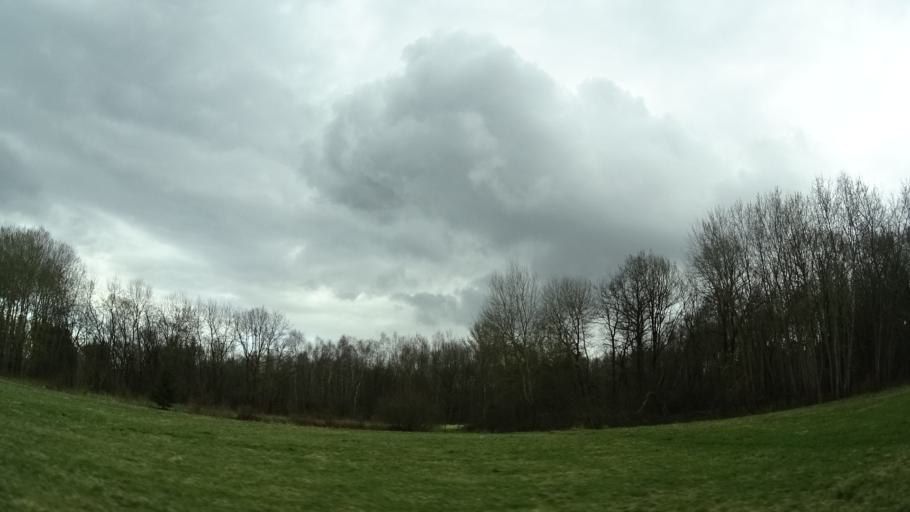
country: DE
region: Rheinland-Pfalz
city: Dorrebach
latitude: 49.9552
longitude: 7.6965
